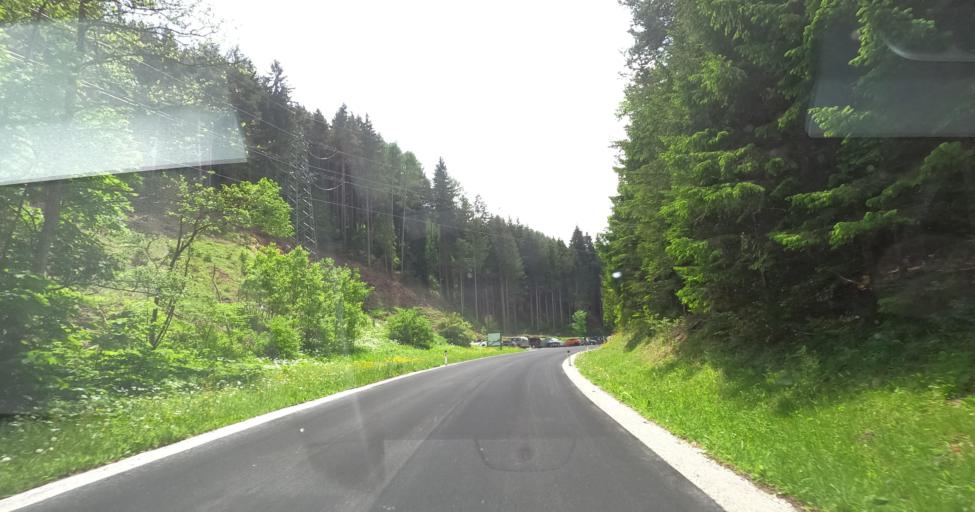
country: AT
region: Tyrol
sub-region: Politischer Bezirk Innsbruck Land
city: Patsch
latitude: 47.2162
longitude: 11.4204
